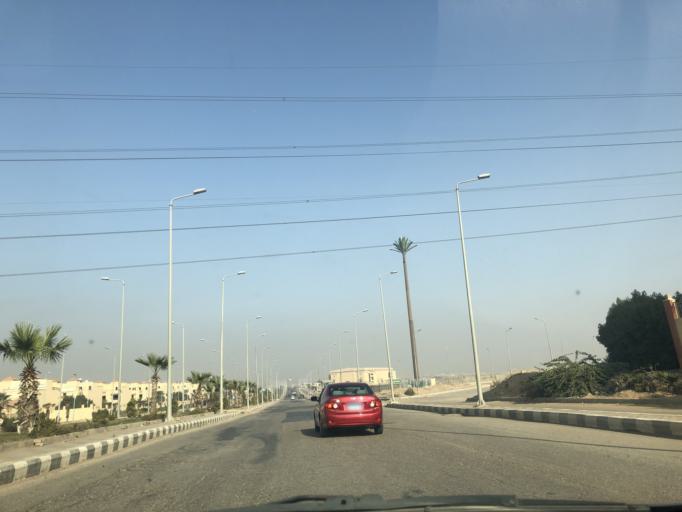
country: EG
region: Al Jizah
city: Madinat Sittah Uktubar
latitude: 29.9485
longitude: 31.0678
